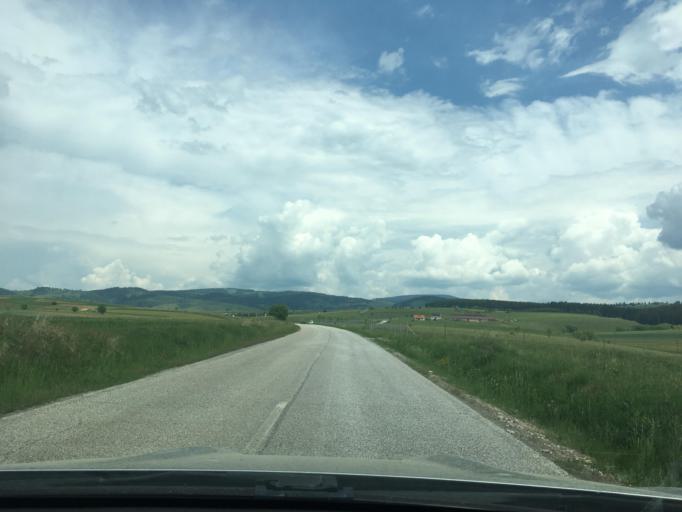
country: RO
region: Harghita
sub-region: Comuna Ditrau
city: Ditrau
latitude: 46.8394
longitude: 25.4965
